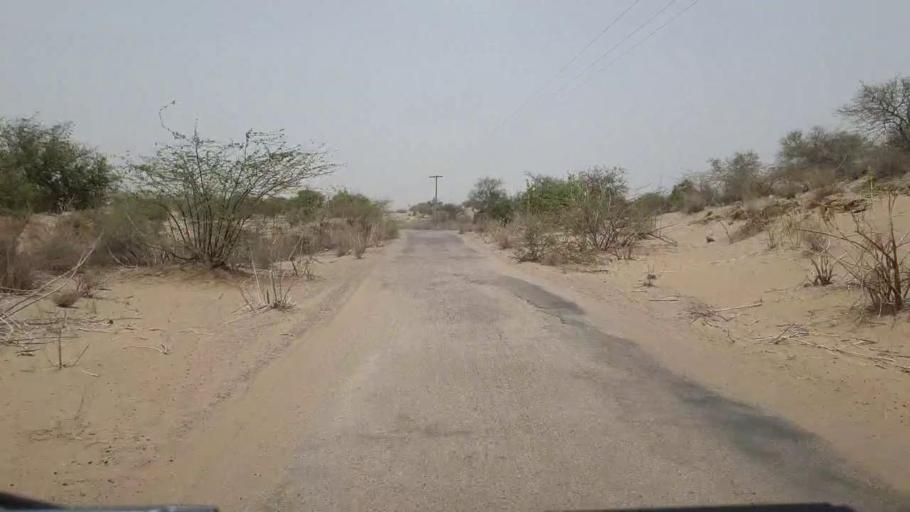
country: PK
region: Sindh
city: Naukot
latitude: 24.7479
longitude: 69.5505
